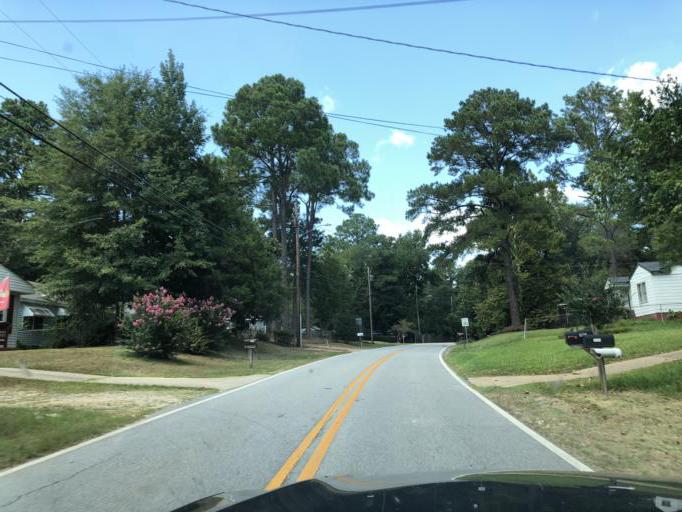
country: US
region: Georgia
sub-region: Muscogee County
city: Columbus
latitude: 32.4859
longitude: -84.9181
